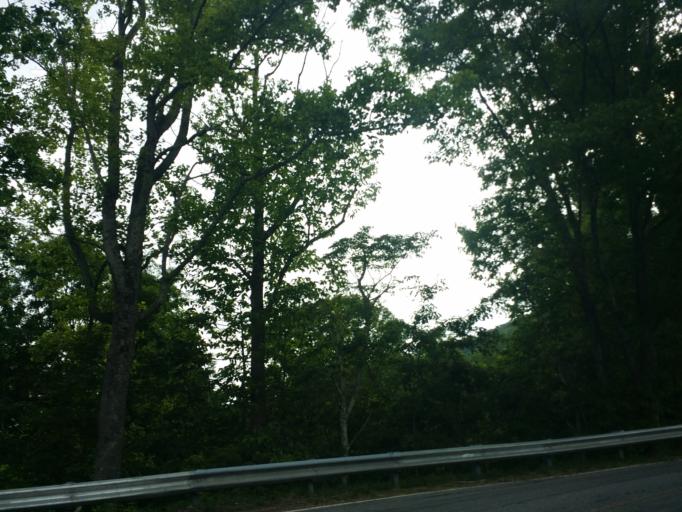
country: US
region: North Carolina
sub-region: Madison County
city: Marshall
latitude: 35.7048
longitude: -82.8246
